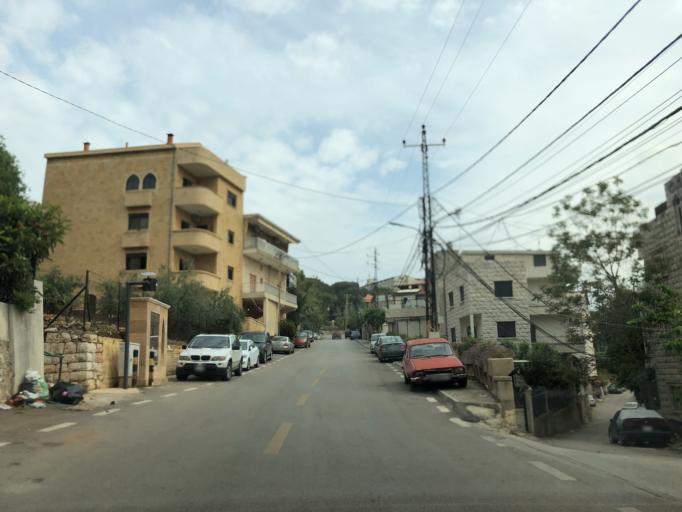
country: LB
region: Mont-Liban
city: Jdaidet el Matn
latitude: 33.8647
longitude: 35.6054
